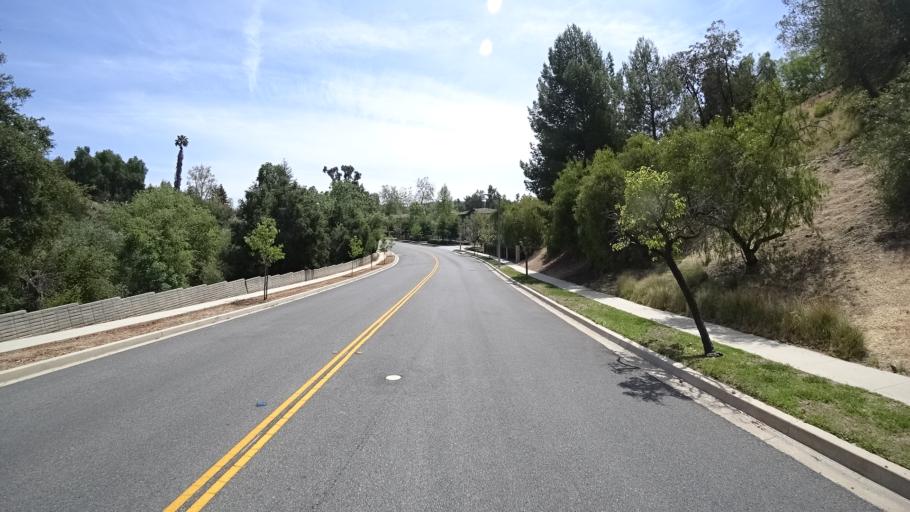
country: US
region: California
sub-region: Ventura County
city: Casa Conejo
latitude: 34.1902
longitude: -118.8892
